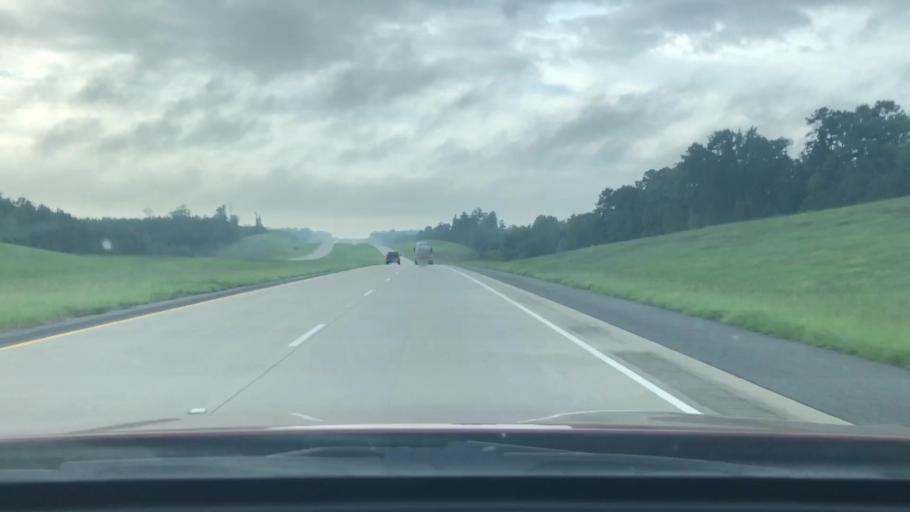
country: US
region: Louisiana
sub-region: Caddo Parish
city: Vivian
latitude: 32.9769
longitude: -93.9096
